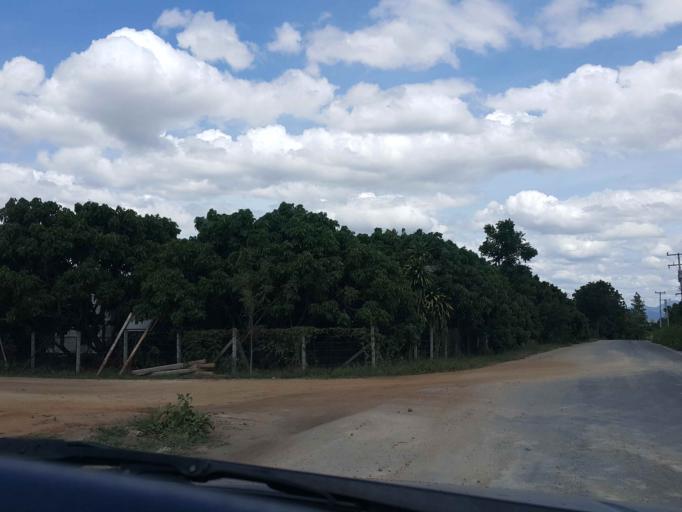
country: TH
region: Chiang Mai
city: Doi Lo
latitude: 18.4777
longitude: 98.7482
